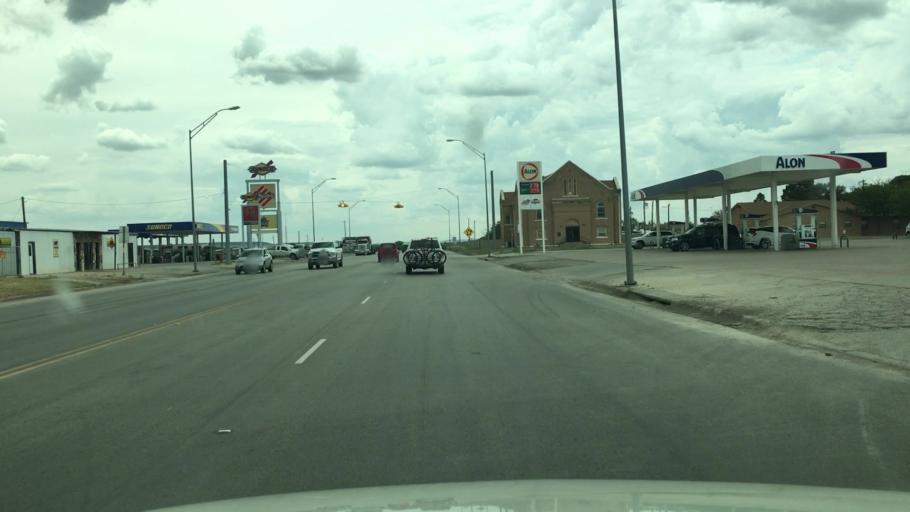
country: US
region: Texas
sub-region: Sterling County
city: Sterling City
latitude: 31.8367
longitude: -100.9929
